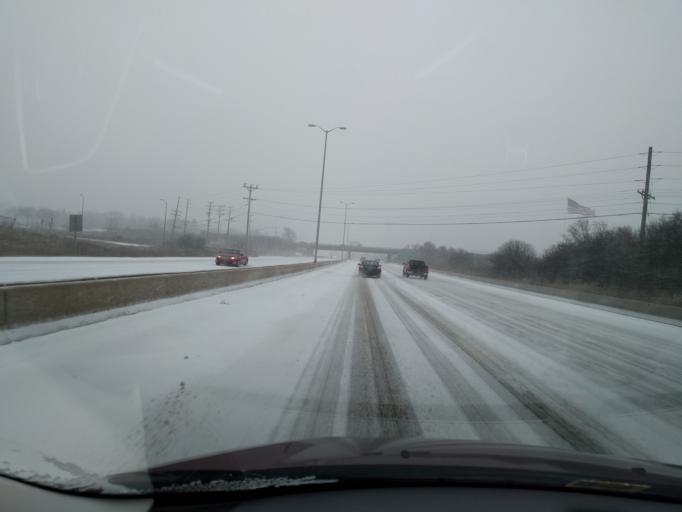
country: US
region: Wisconsin
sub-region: Waukesha County
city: Butler
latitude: 43.1493
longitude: -88.0529
